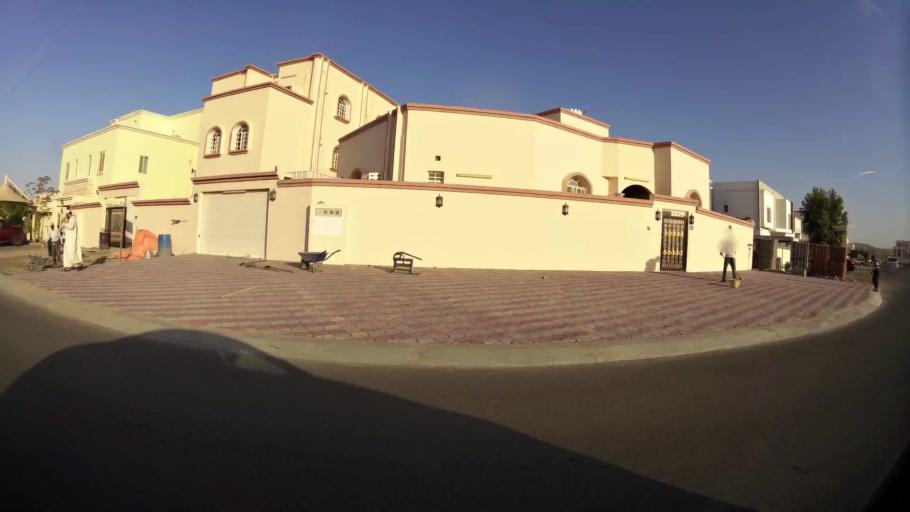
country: OM
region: Muhafazat Masqat
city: As Sib al Jadidah
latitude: 23.5930
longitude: 58.1384
